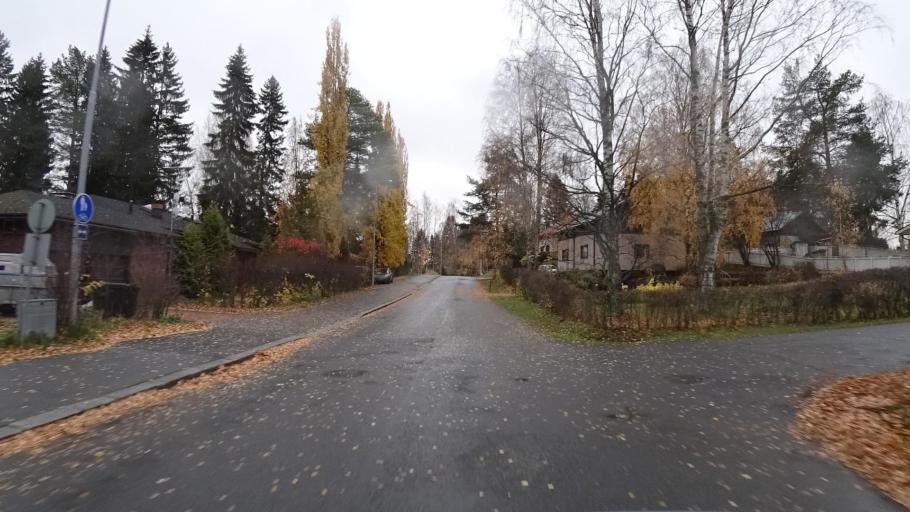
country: FI
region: Northern Savo
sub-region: Kuopio
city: Kuopio
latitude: 62.9283
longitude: 27.6944
